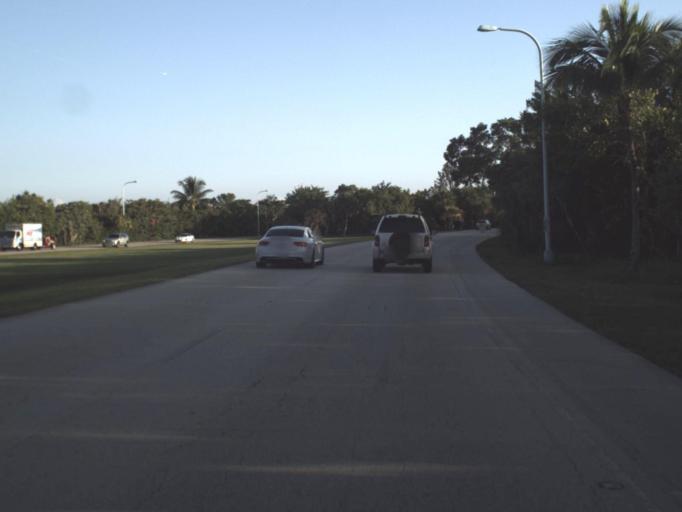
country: US
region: Florida
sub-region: Miami-Dade County
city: Key Biscayne
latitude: 25.7239
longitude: -80.1518
